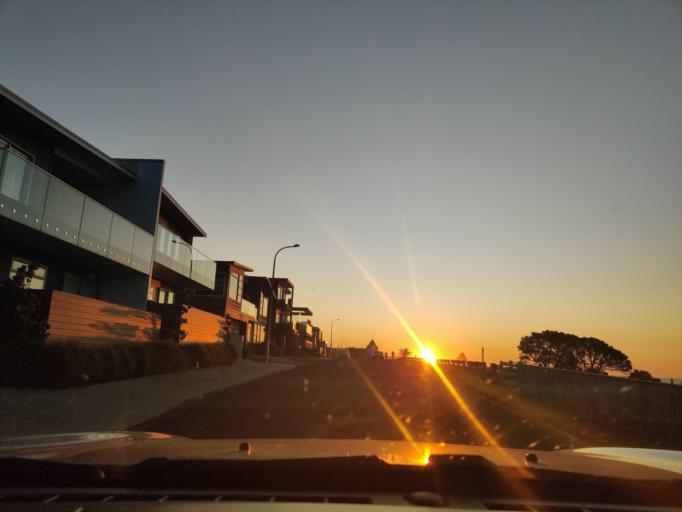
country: NZ
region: Taranaki
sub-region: New Plymouth District
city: New Plymouth
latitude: -39.0512
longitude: 174.0836
